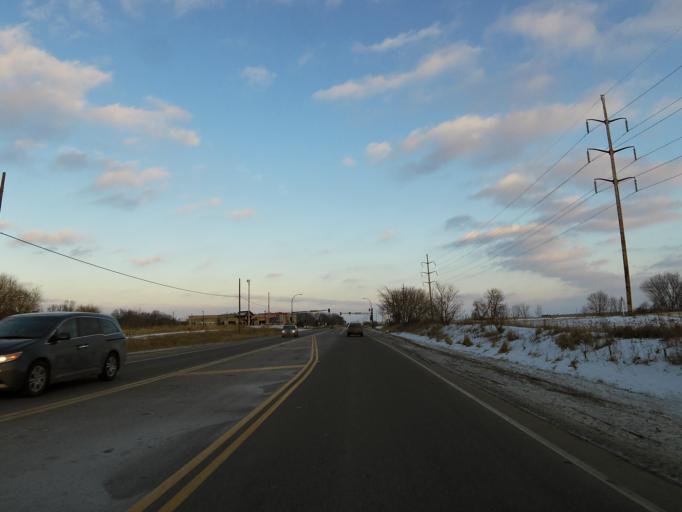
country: US
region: Minnesota
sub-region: Dakota County
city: Lakeville
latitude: 44.6380
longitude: -93.2707
